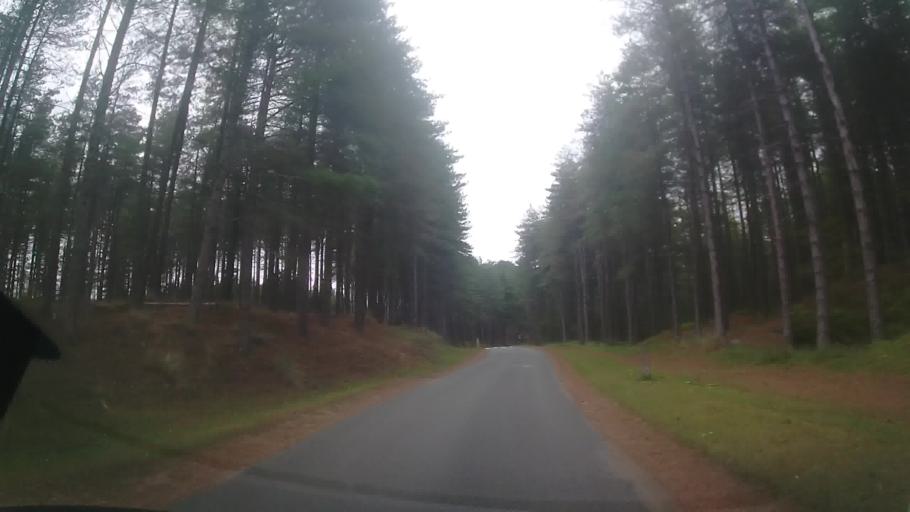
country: GB
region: Wales
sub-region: Gwynedd
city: Caernarfon
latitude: 53.1465
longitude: -4.3855
